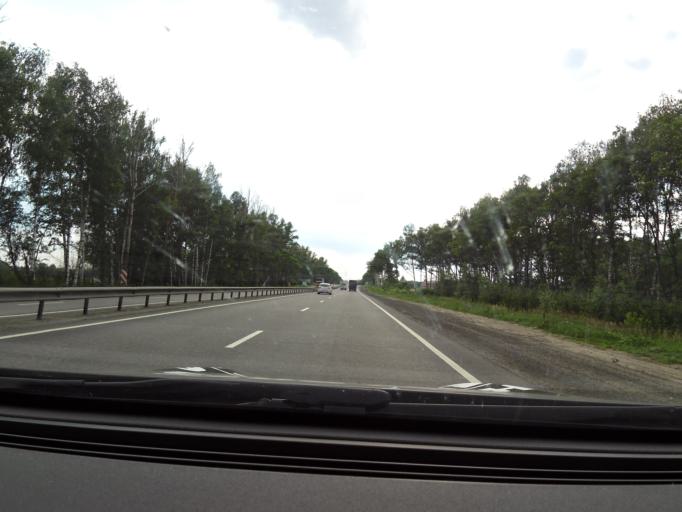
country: RU
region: Vladimir
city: Gorokhovets
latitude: 56.1611
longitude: 42.6008
